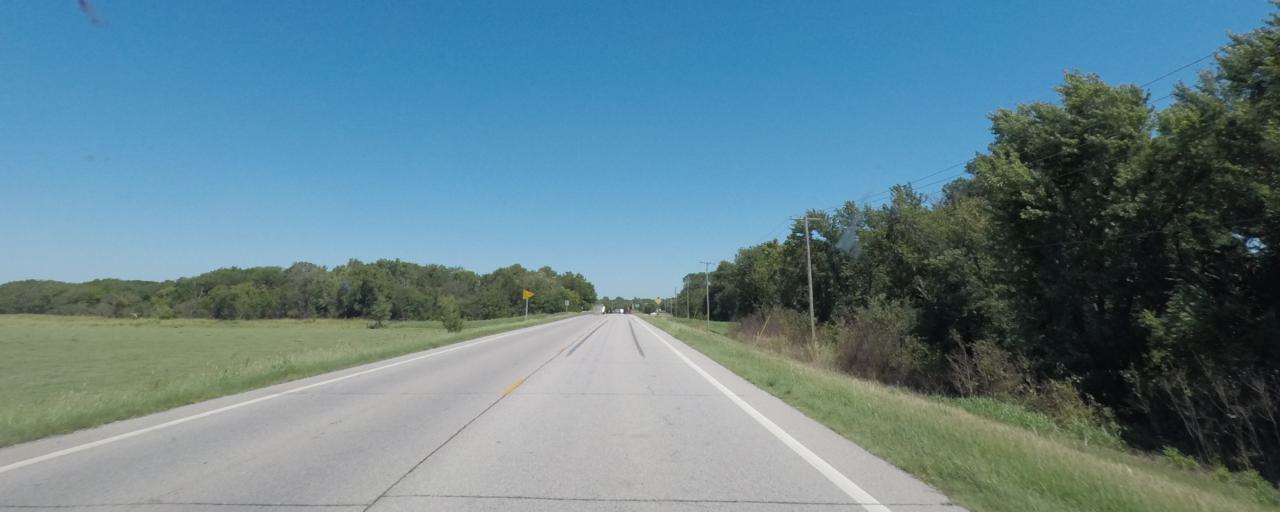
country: US
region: Kansas
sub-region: Sumner County
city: Wellington
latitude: 37.2481
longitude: -97.4034
